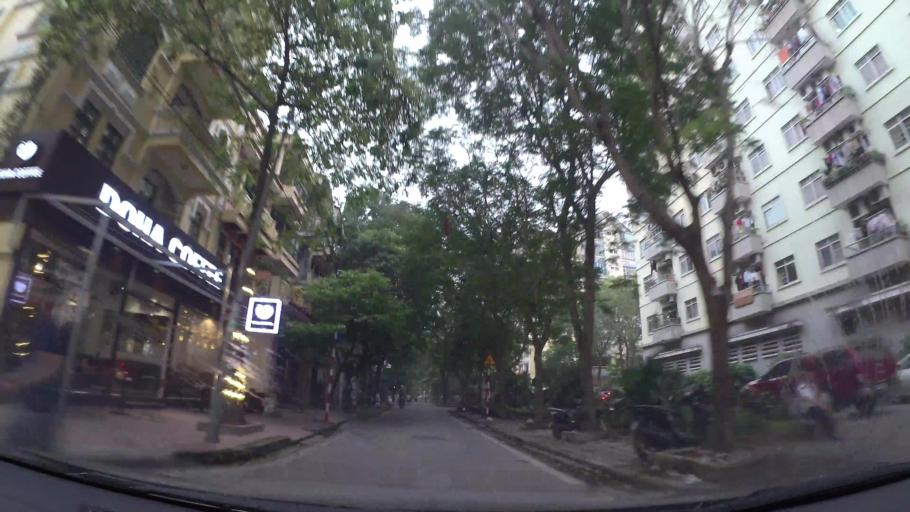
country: VN
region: Ha Noi
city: Thanh Xuan
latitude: 20.9864
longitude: 105.8284
